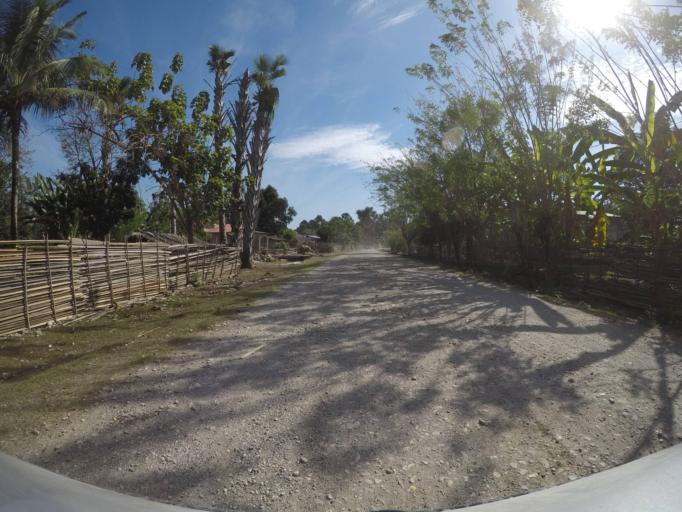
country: TL
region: Bobonaro
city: Maliana
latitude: -8.8661
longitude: 125.2144
